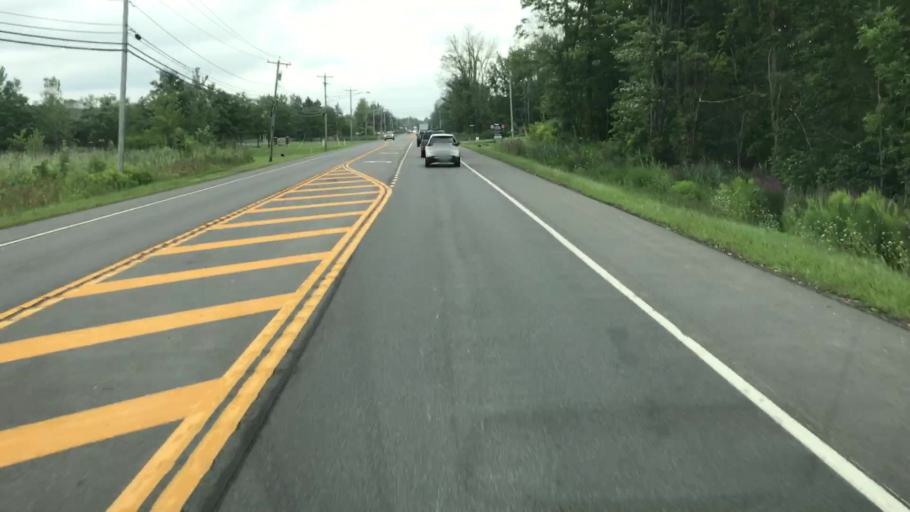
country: US
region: New York
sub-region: Onondaga County
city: Liverpool
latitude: 43.1863
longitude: -76.2099
